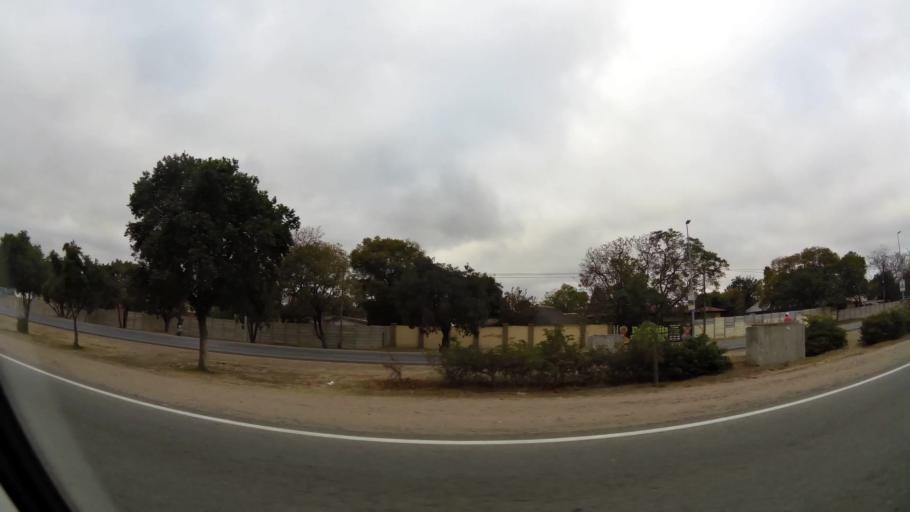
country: ZA
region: Limpopo
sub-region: Capricorn District Municipality
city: Polokwane
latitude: -23.9185
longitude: 29.4405
